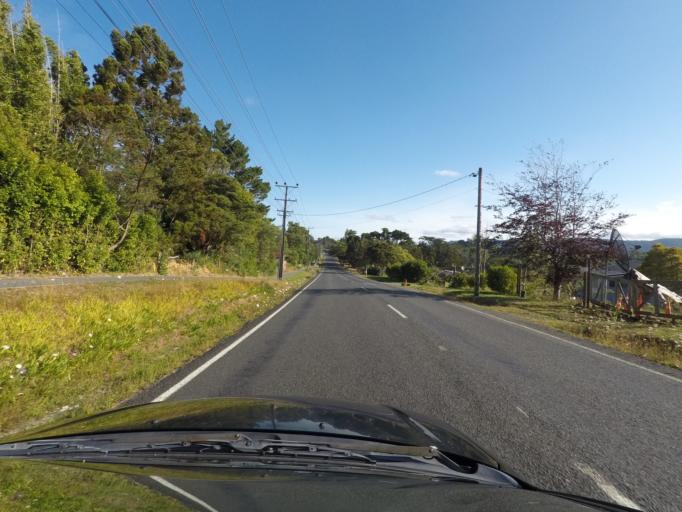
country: NZ
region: Auckland
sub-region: Auckland
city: Rosebank
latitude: -36.8765
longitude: 174.5971
